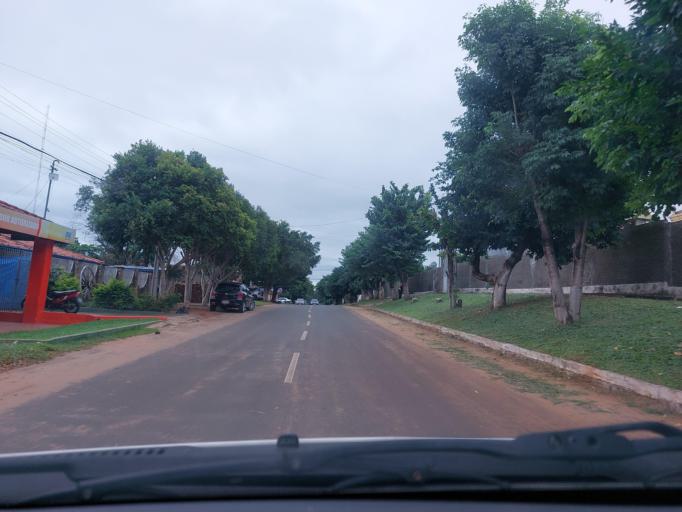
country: PY
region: San Pedro
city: Guayaybi
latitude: -24.6699
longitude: -56.4435
